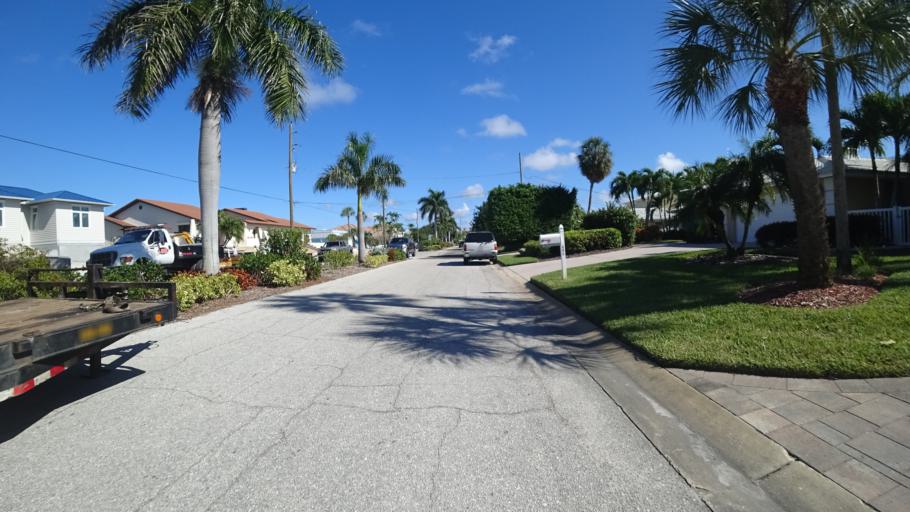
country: US
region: Florida
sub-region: Manatee County
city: Anna Maria
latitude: 27.5250
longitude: -82.7129
